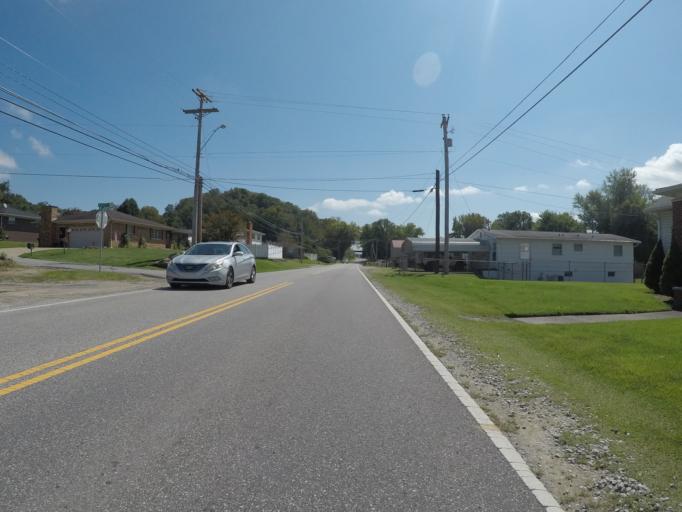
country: US
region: West Virginia
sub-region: Wayne County
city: Kenova
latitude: 38.4101
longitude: -82.5751
